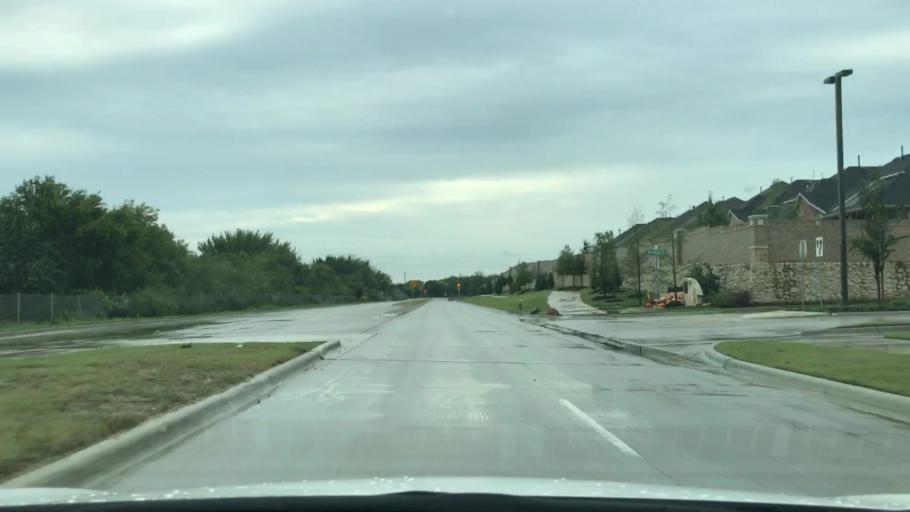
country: US
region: Texas
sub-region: Dallas County
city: Coppell
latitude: 32.9063
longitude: -97.0037
